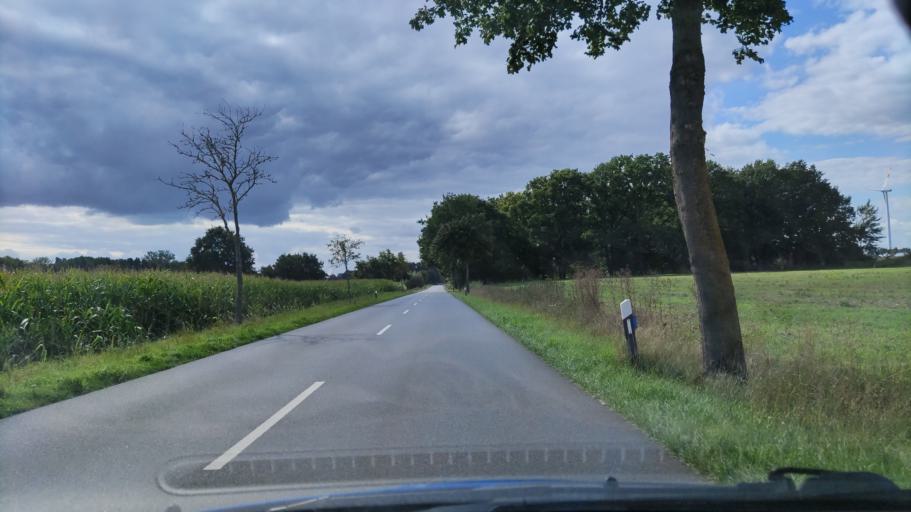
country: DE
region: Lower Saxony
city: Oetzen
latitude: 53.0180
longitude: 10.6428
